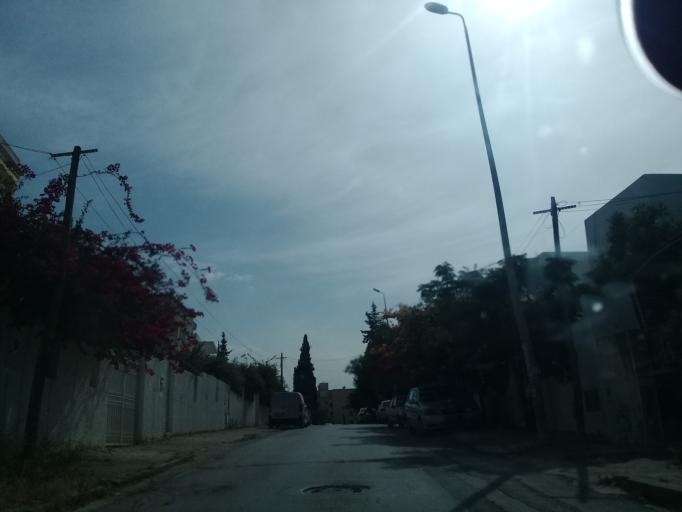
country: TN
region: Tunis
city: Tunis
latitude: 36.8517
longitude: 10.1597
